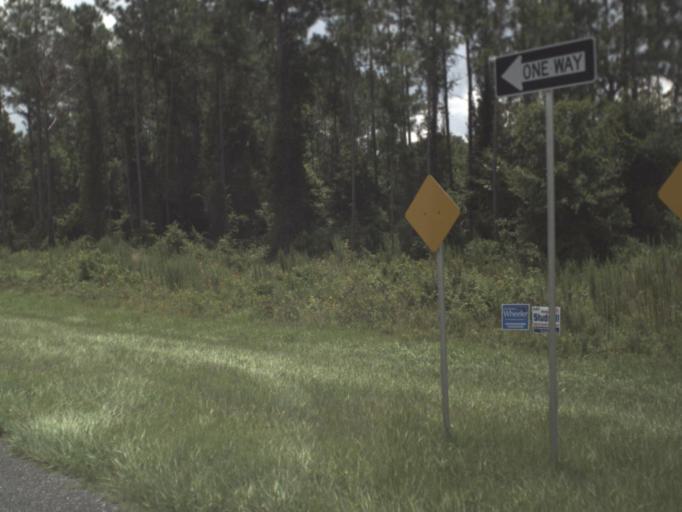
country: US
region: Florida
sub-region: Levy County
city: Bronson
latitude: 29.4765
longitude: -82.6848
